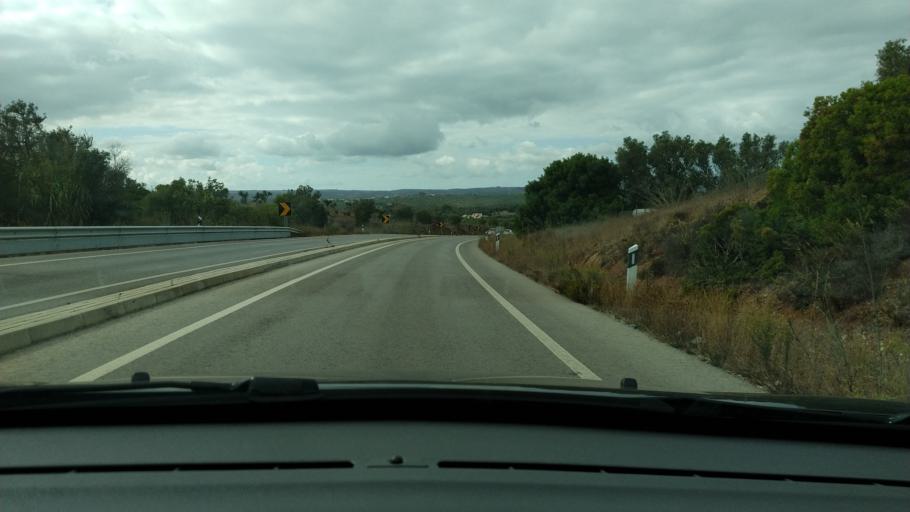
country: PT
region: Faro
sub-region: Lagos
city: Lagos
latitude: 37.0977
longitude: -8.7431
